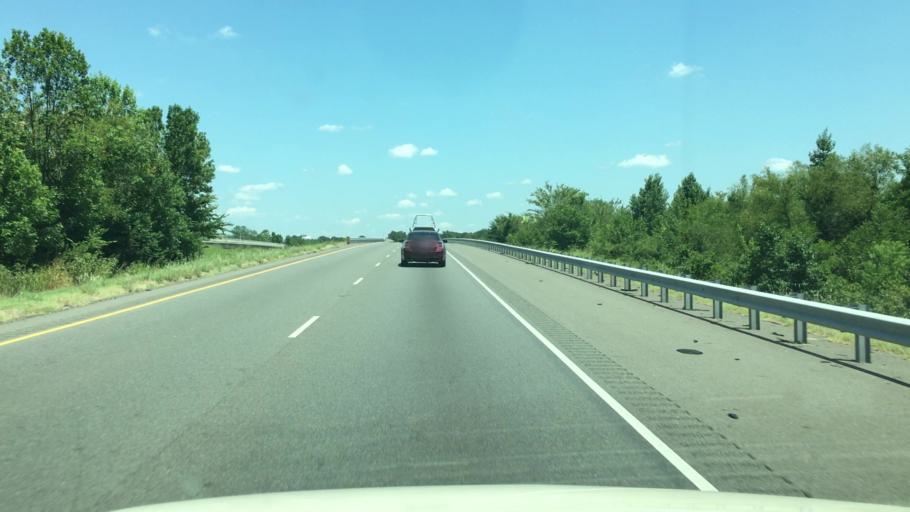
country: US
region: Arkansas
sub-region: Hempstead County
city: Hope
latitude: 33.6734
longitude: -93.6219
